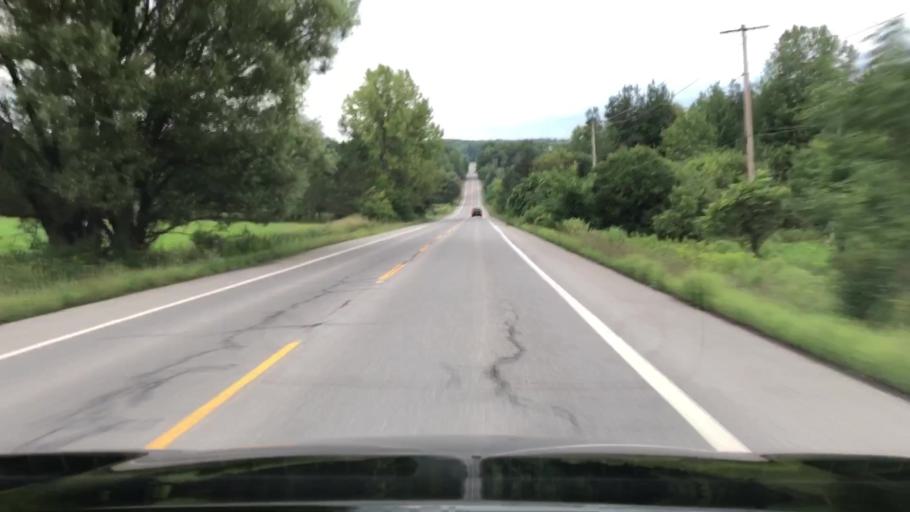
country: US
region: New York
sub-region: Erie County
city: Orchard Park
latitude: 42.7647
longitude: -78.6969
